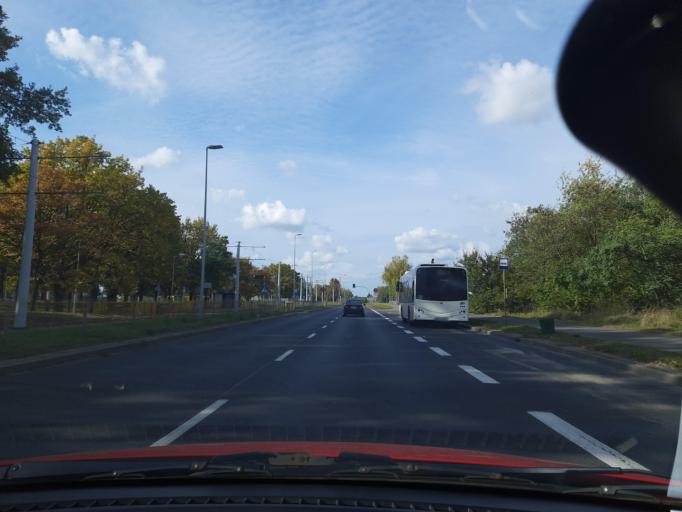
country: PL
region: Kujawsko-Pomorskie
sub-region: Powiat torunski
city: Wielka Nieszawka
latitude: 53.0156
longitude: 18.5494
